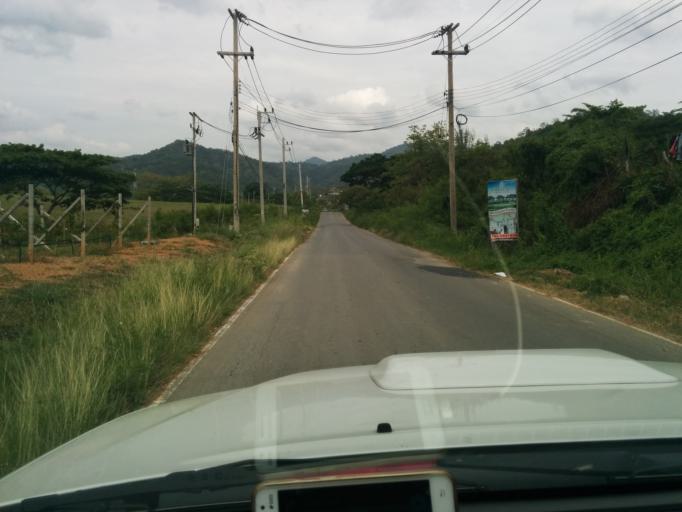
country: TH
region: Sara Buri
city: Muak Lek
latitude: 14.5636
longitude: 101.2504
